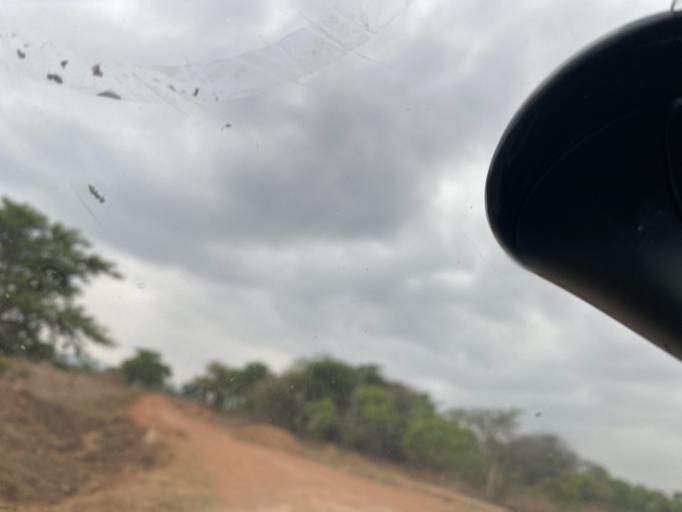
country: ZM
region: Lusaka
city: Chongwe
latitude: -15.2324
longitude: 28.7233
